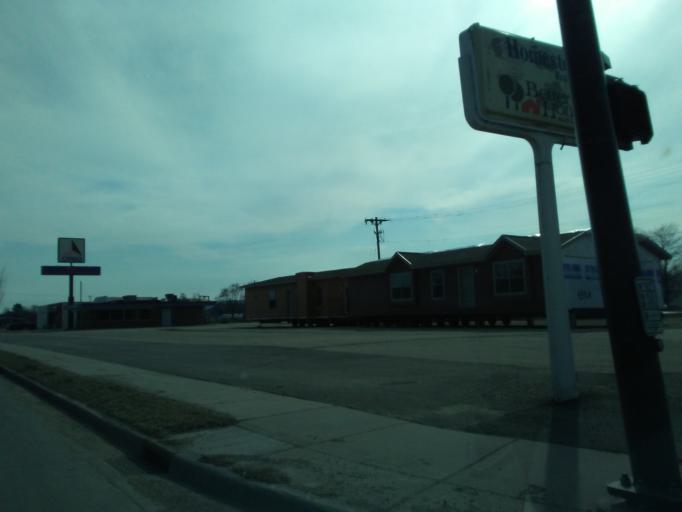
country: US
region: Wisconsin
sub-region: Crawford County
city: Prairie du Chien
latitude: 43.0464
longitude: -91.1410
